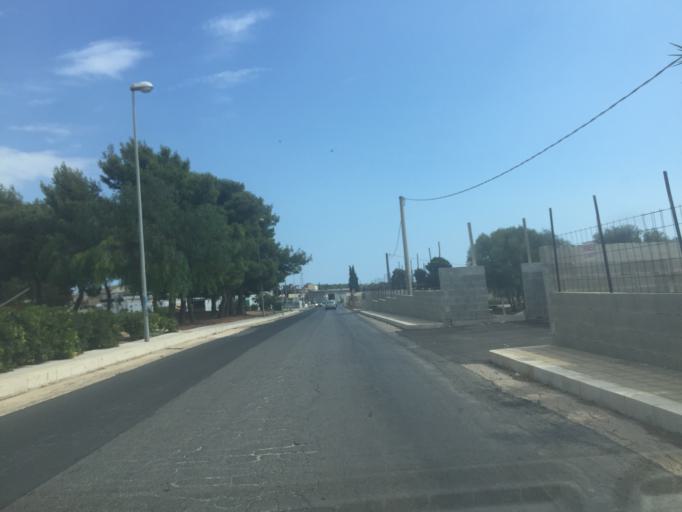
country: IT
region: Sicily
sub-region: Ragusa
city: Santa Croce Camerina
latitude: 36.8233
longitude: 14.5191
